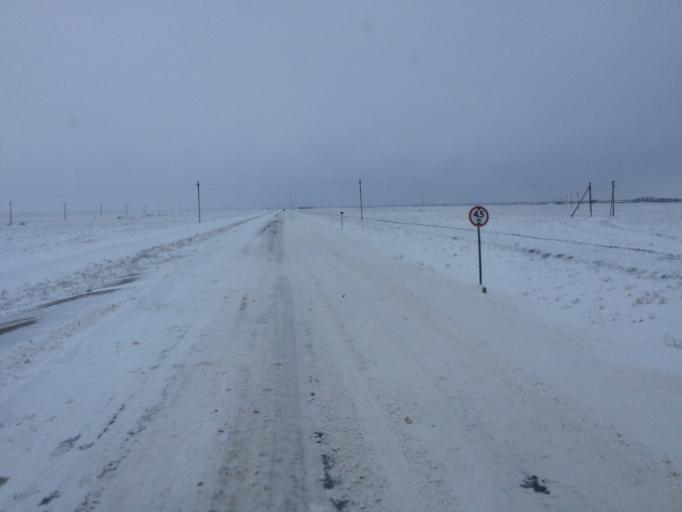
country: KZ
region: Atyrau
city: Inderbor
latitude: 49.3556
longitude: 51.7700
